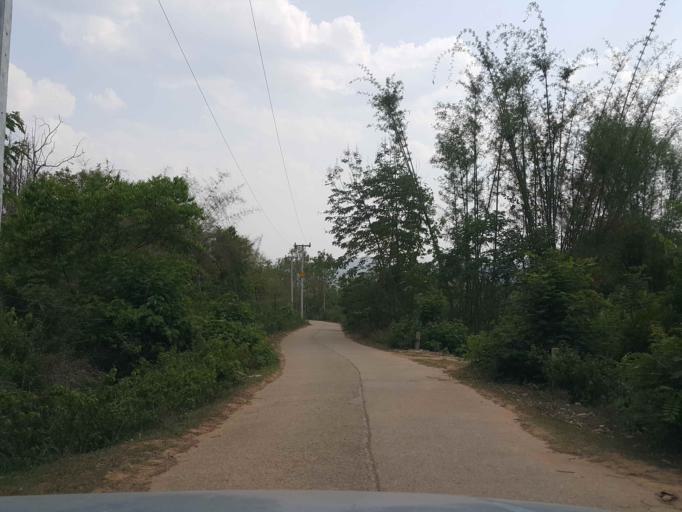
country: TH
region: Chiang Mai
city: Wiang Haeng
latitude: 19.4037
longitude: 98.7229
